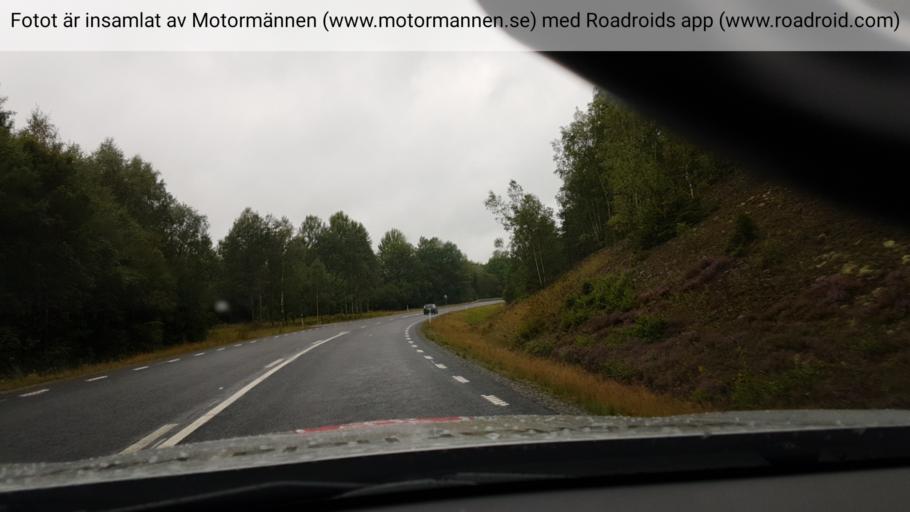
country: SE
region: Vaestra Goetaland
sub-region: Dals-Ed Kommun
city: Ed
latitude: 58.9066
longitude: 12.0001
